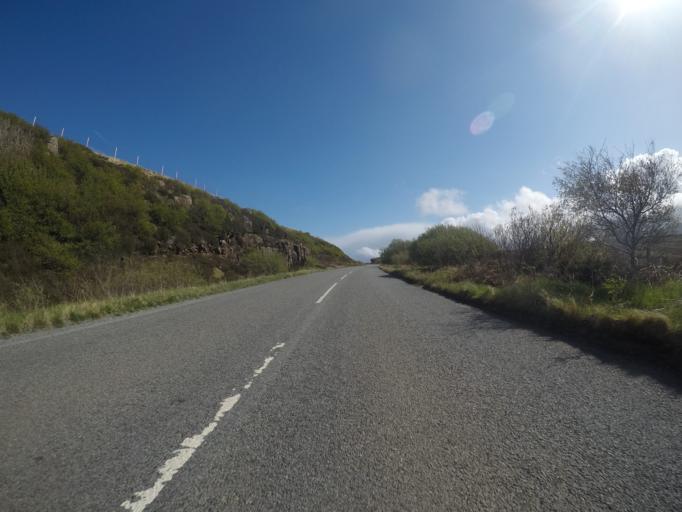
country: GB
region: Scotland
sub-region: Highland
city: Portree
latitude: 57.6062
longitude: -6.1718
